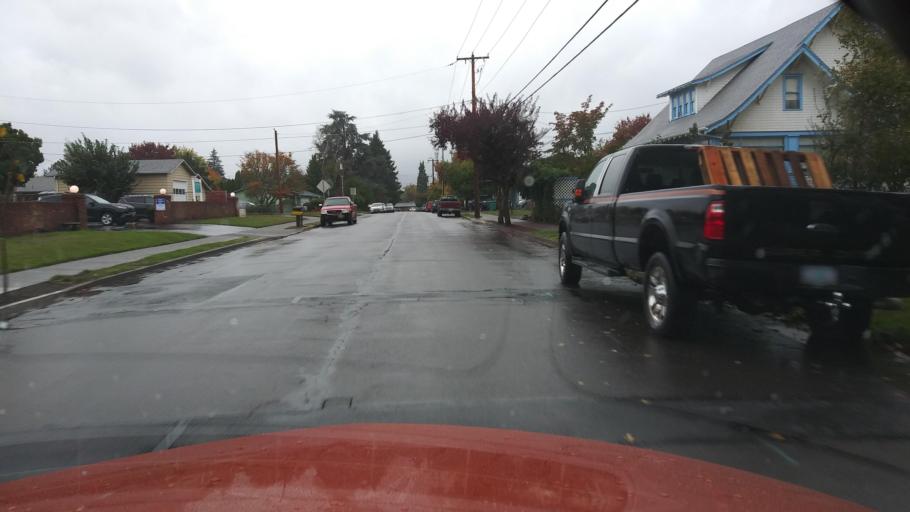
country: US
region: Oregon
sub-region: Washington County
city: Forest Grove
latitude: 45.5224
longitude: -123.0959
